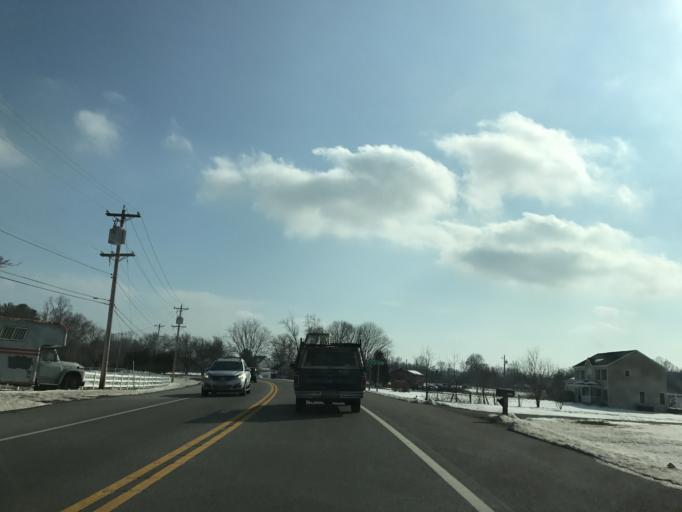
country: US
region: Maryland
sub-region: Harford County
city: South Bel Air
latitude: 39.6430
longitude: -76.2689
